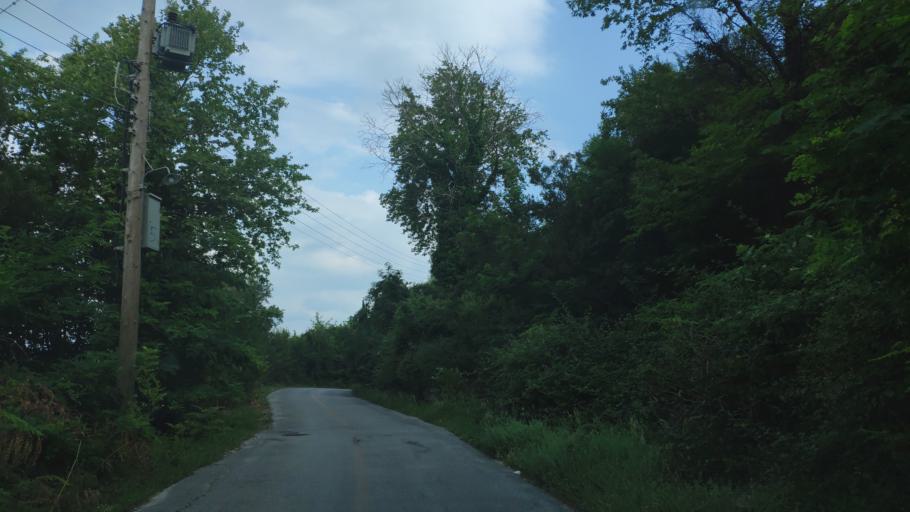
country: GR
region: Epirus
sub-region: Nomos Artas
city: Agios Dimitrios
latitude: 39.3811
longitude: 21.0255
